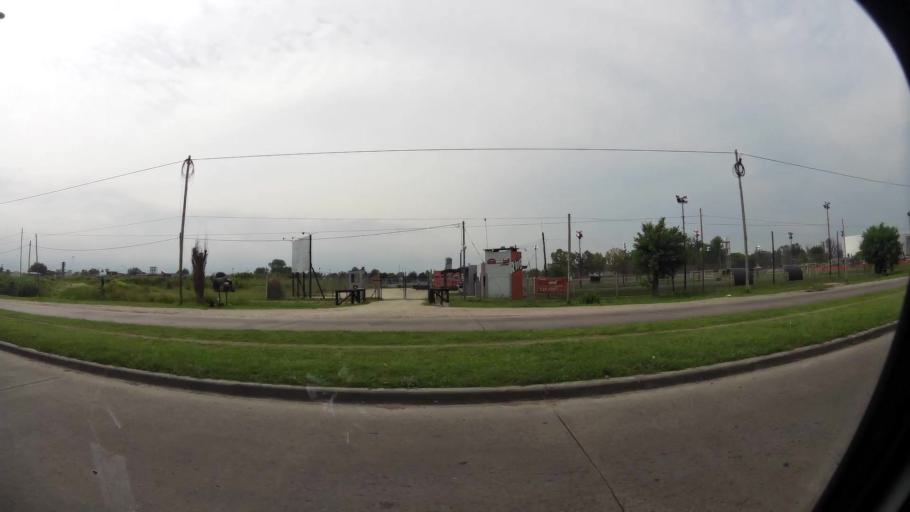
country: AR
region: Buenos Aires
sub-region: Partido de La Plata
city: La Plata
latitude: -34.9027
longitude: -57.9963
